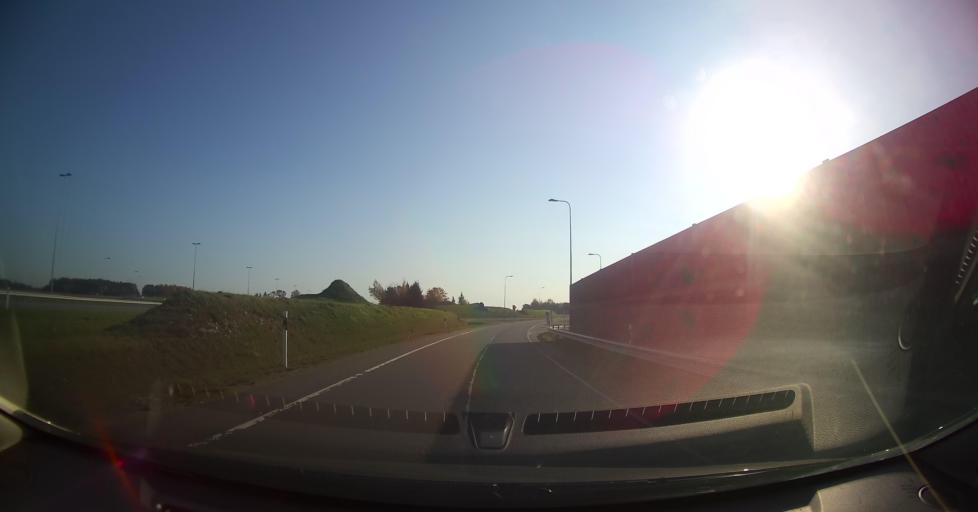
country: EE
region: Harju
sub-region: Rae vald
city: Vaida
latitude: 59.1822
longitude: 25.1082
